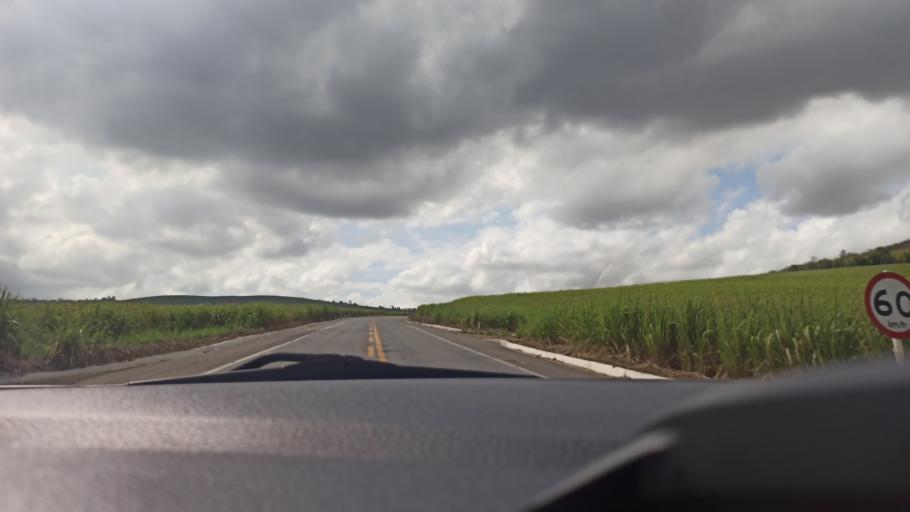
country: BR
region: Pernambuco
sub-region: Timbauba
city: Timbauba
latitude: -7.5261
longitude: -35.2907
